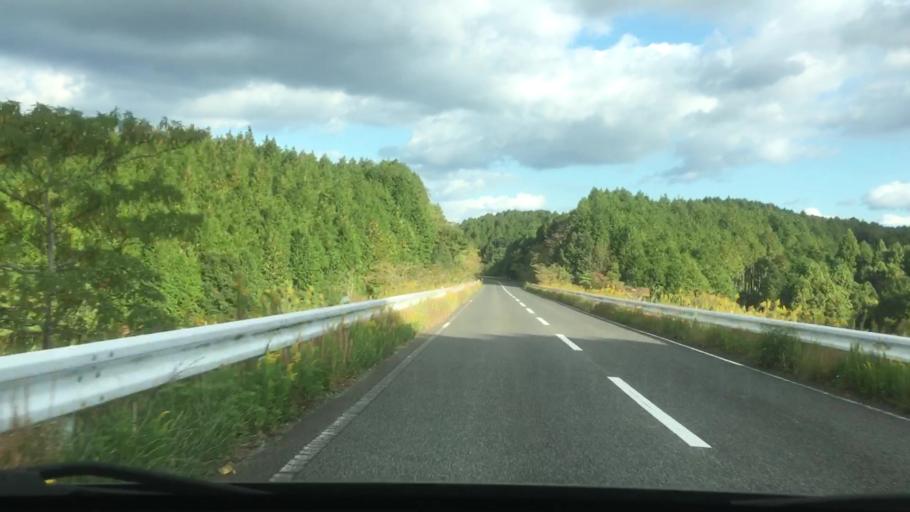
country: JP
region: Nagasaki
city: Sasebo
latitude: 33.0213
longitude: 129.6991
